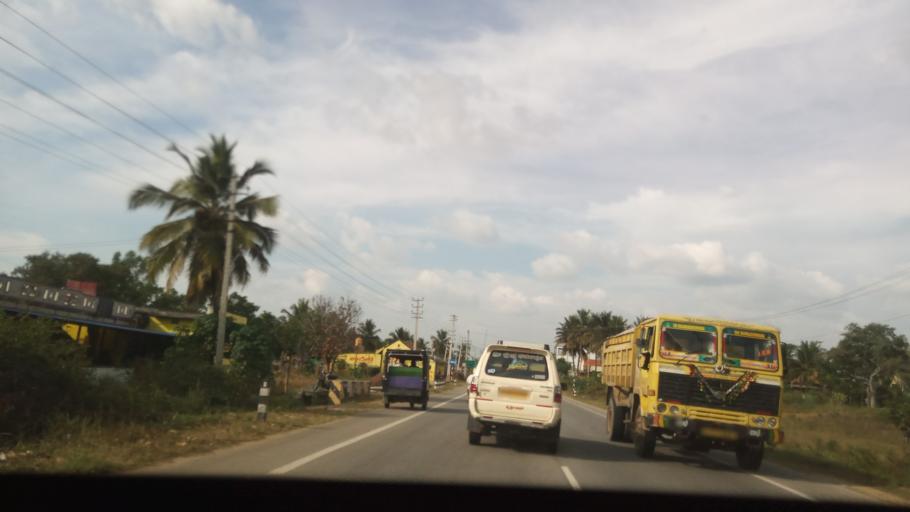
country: IN
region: Karnataka
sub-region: Mandya
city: Maddur
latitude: 12.6800
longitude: 77.0590
